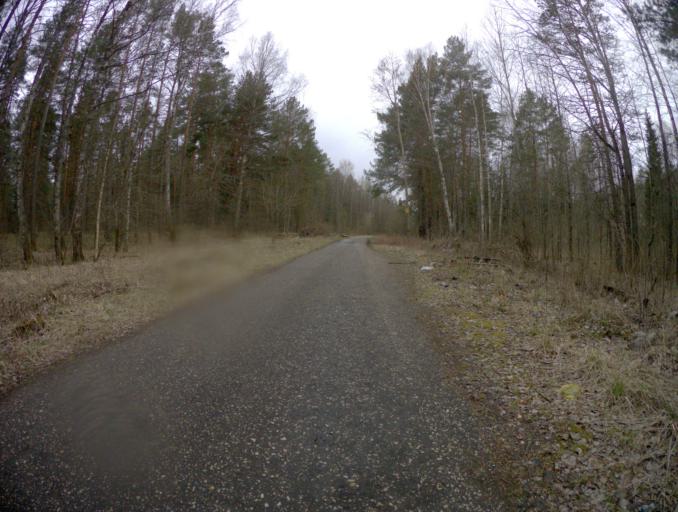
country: RU
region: Vladimir
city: Sudogda
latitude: 55.9736
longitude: 40.8147
